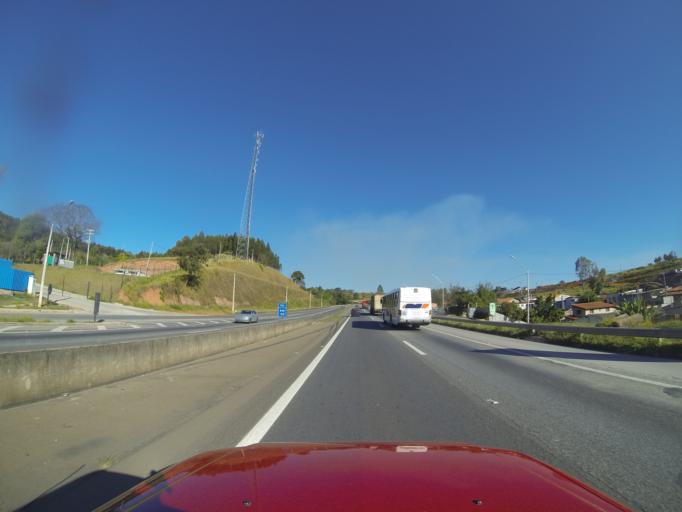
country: BR
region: Sao Paulo
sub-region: Atibaia
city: Atibaia
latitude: -23.0721
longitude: -46.5670
